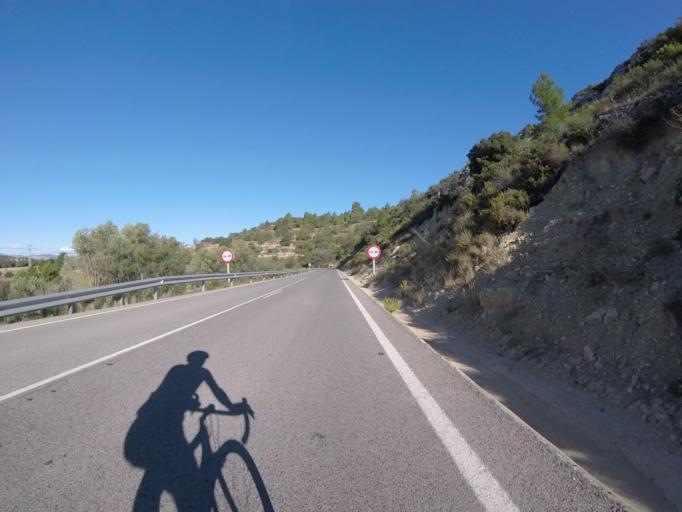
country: ES
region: Valencia
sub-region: Provincia de Castello
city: Cervera del Maestre
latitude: 40.4573
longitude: 0.2658
